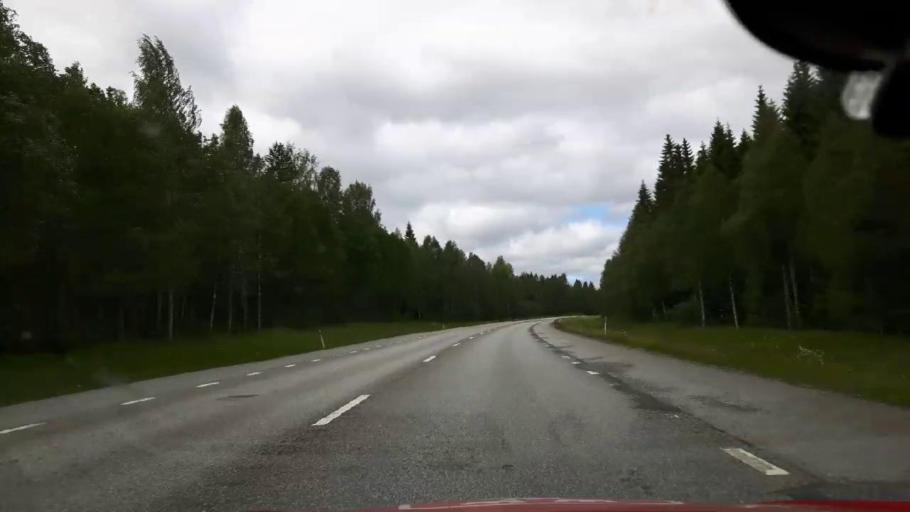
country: SE
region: Jaemtland
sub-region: Braecke Kommun
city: Braecke
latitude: 62.6904
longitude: 15.5469
